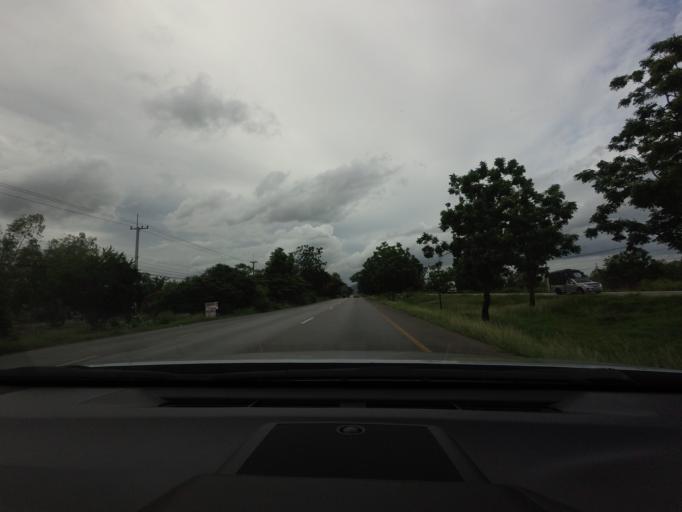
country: TH
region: Phetchaburi
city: Cha-am
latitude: 12.7477
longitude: 99.9307
